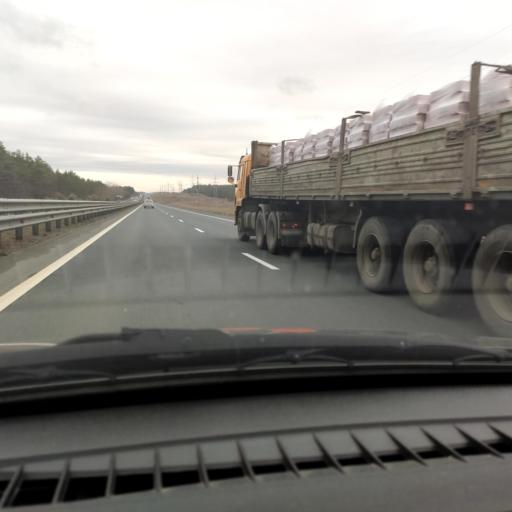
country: RU
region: Samara
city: Povolzhskiy
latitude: 53.5139
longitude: 49.6243
